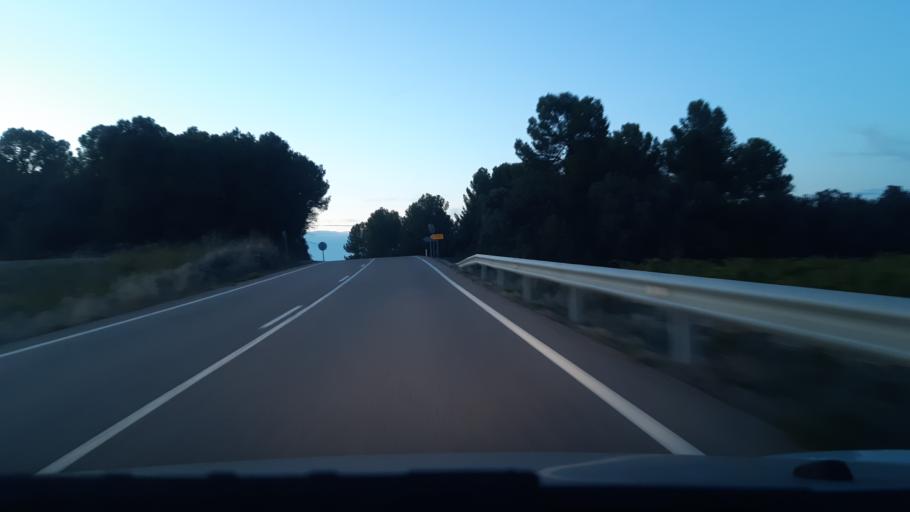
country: ES
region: Aragon
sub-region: Provincia de Teruel
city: Lledo
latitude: 40.9576
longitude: 0.2175
